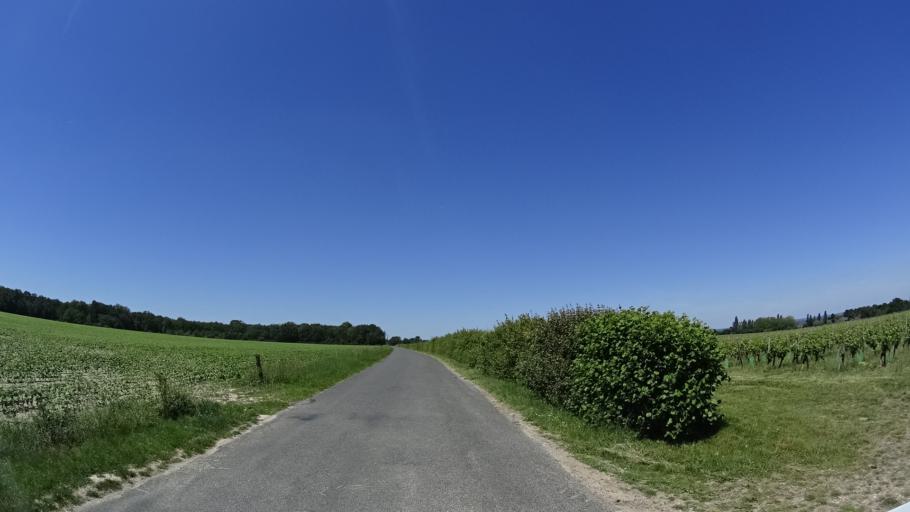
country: FR
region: Pays de la Loire
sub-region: Departement de Maine-et-Loire
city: Chenehutte-Treves-Cunault
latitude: 47.2857
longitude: -0.1410
